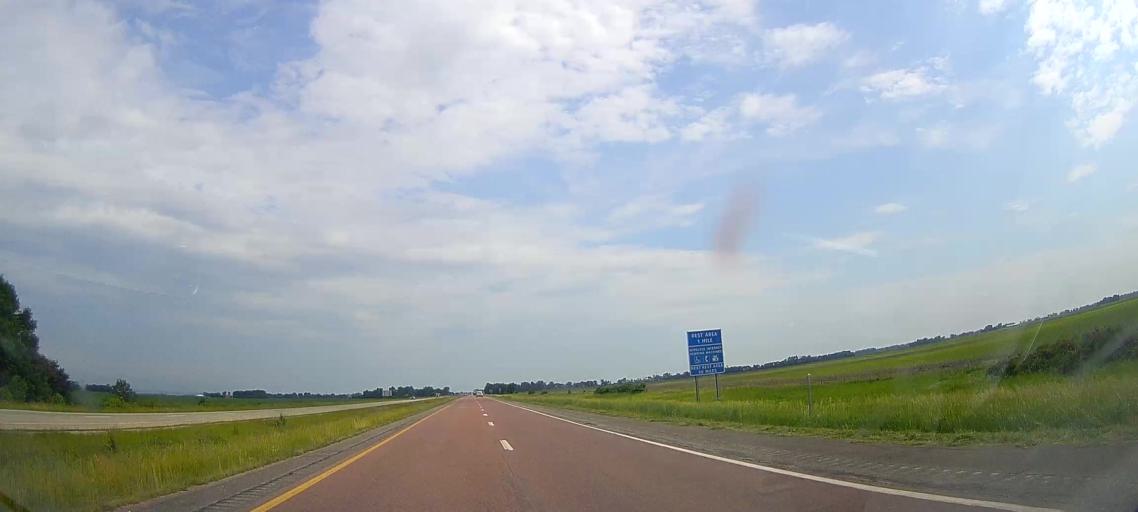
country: US
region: Iowa
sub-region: Monona County
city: Onawa
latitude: 42.0066
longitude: -96.1171
